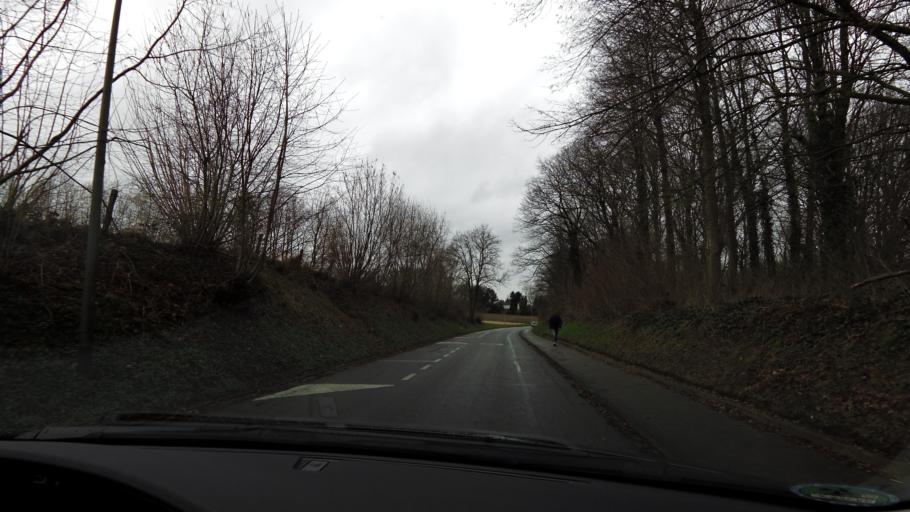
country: NL
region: Limburg
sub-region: Gemeente Beek
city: Beek
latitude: 50.9324
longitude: 5.7876
